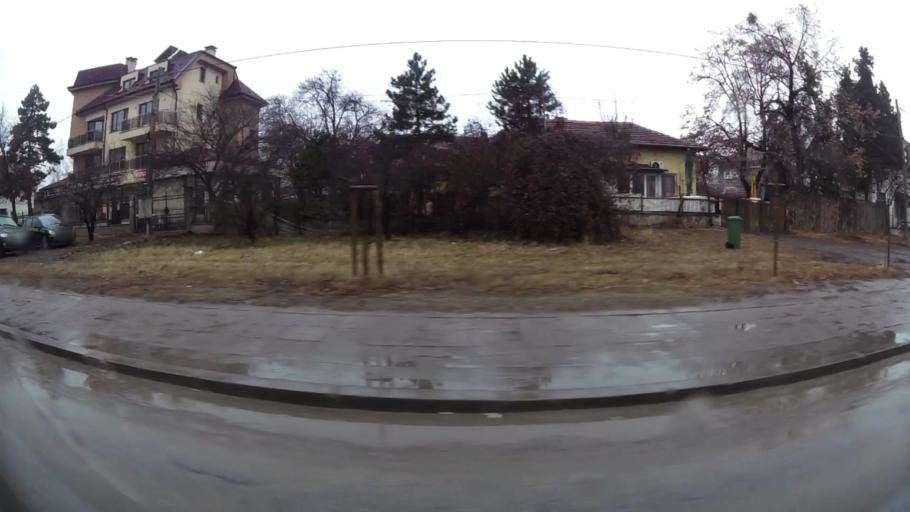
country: BG
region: Sofia-Capital
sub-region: Stolichna Obshtina
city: Sofia
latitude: 42.6319
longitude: 23.4090
